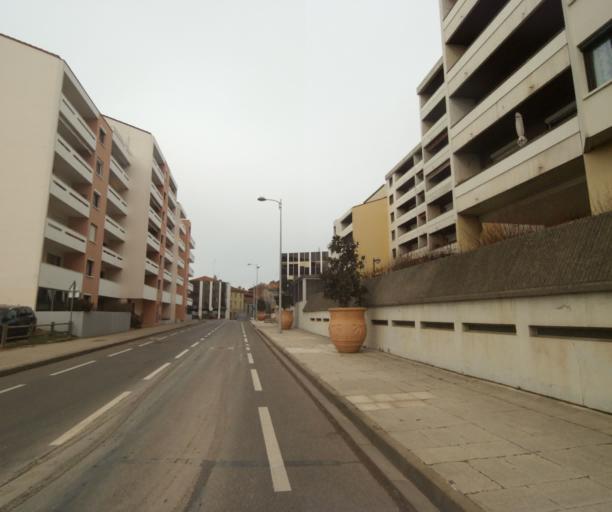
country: FR
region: Rhone-Alpes
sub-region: Departement de la Loire
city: Roanne
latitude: 46.0333
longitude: 4.0717
